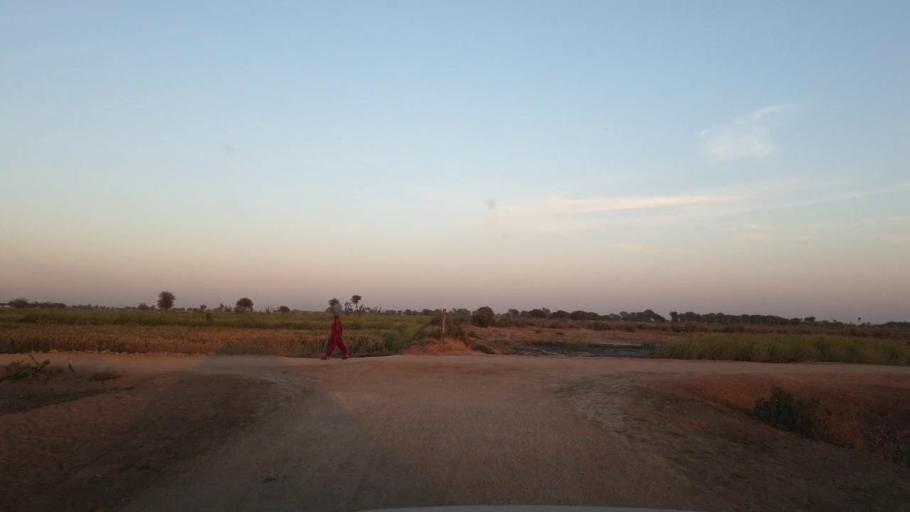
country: PK
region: Sindh
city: Samaro
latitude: 25.1508
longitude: 69.4254
